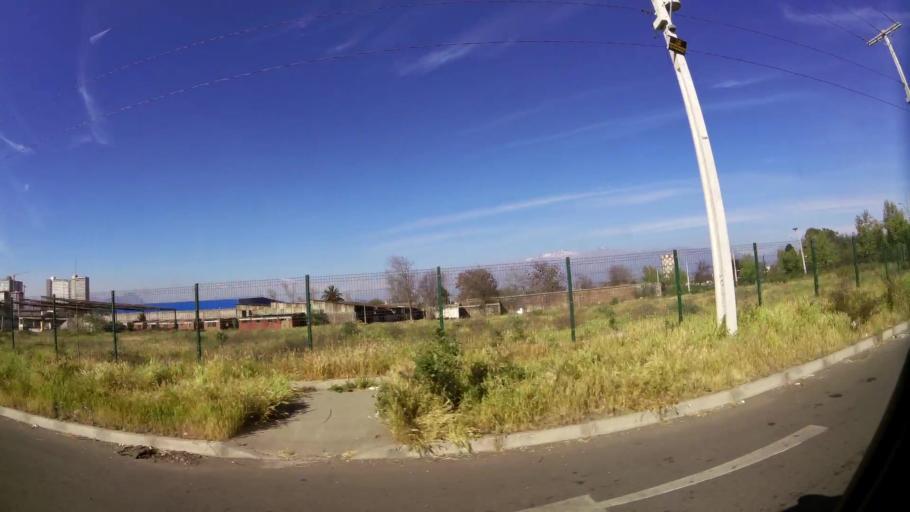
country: CL
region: Santiago Metropolitan
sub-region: Provincia de Santiago
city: Lo Prado
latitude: -33.4640
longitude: -70.6952
